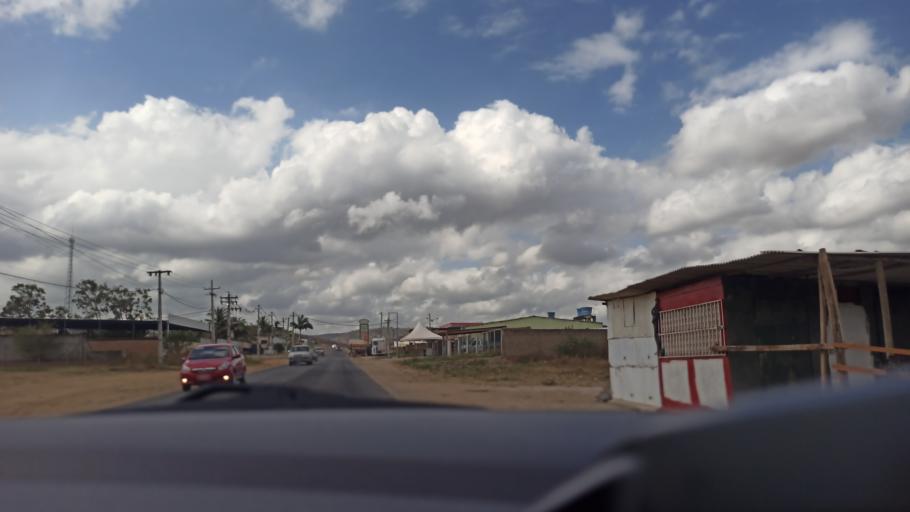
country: BR
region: Pernambuco
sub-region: Timbauba
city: Timbauba
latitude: -7.4939
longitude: -35.2972
